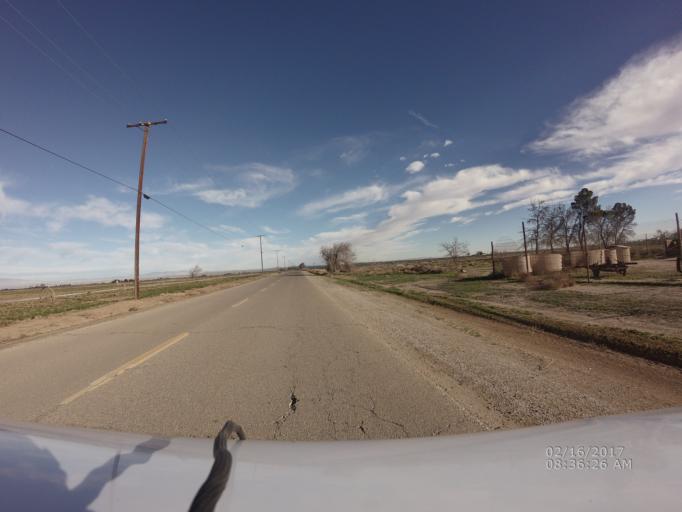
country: US
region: California
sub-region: Los Angeles County
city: Lancaster
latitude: 34.7402
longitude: -118.0053
